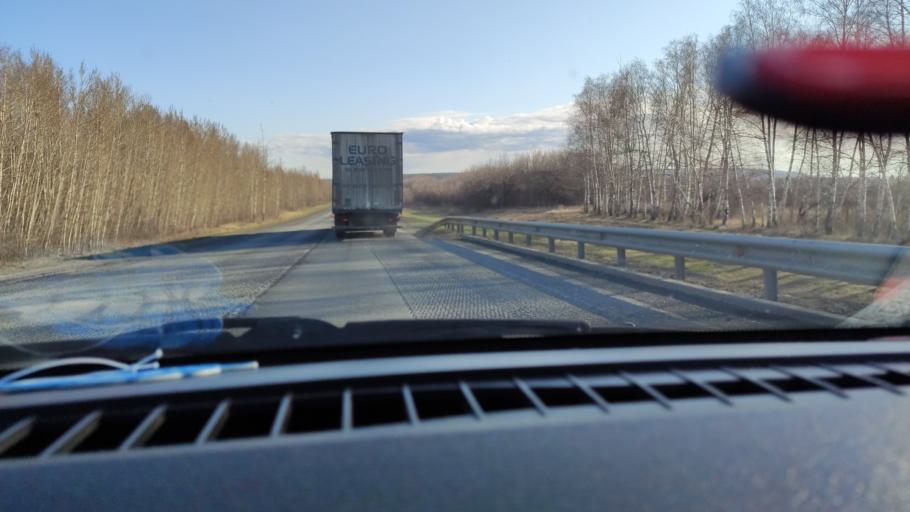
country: RU
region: Saratov
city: Dukhovnitskoye
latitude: 52.6923
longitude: 48.2453
